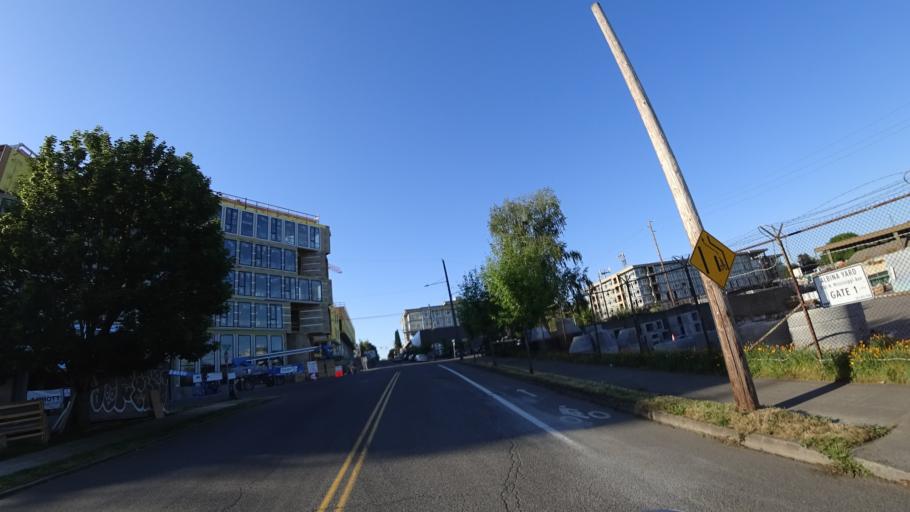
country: US
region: Oregon
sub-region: Multnomah County
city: Portland
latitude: 45.5463
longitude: -122.6756
